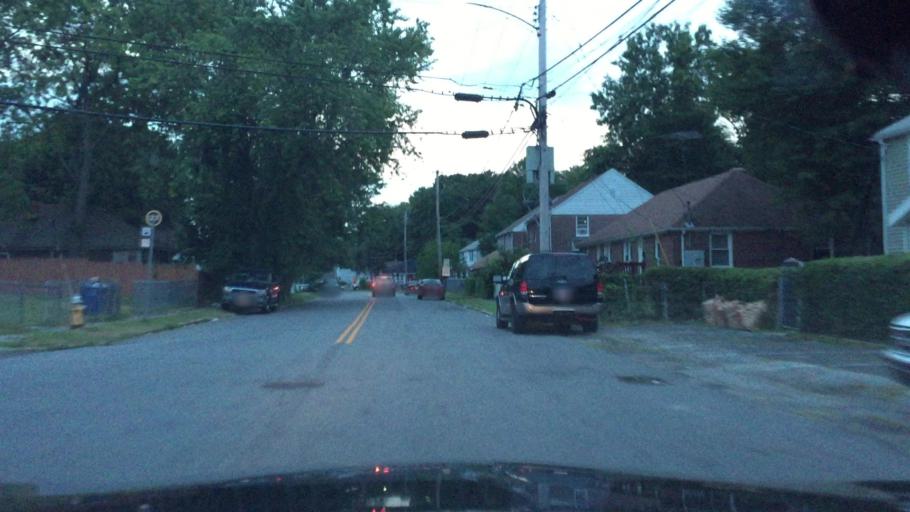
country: US
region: Connecticut
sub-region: Fairfield County
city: Stratford
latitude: 41.2025
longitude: -73.1609
